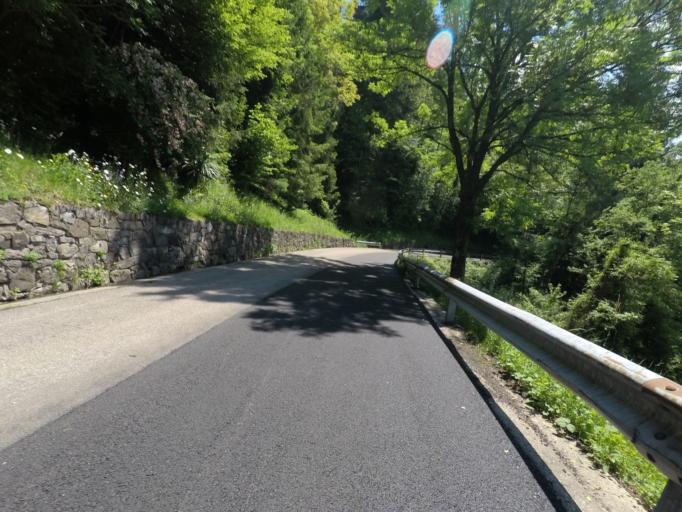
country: IT
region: Friuli Venezia Giulia
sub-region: Provincia di Udine
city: Raveo
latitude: 46.4354
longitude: 12.8876
